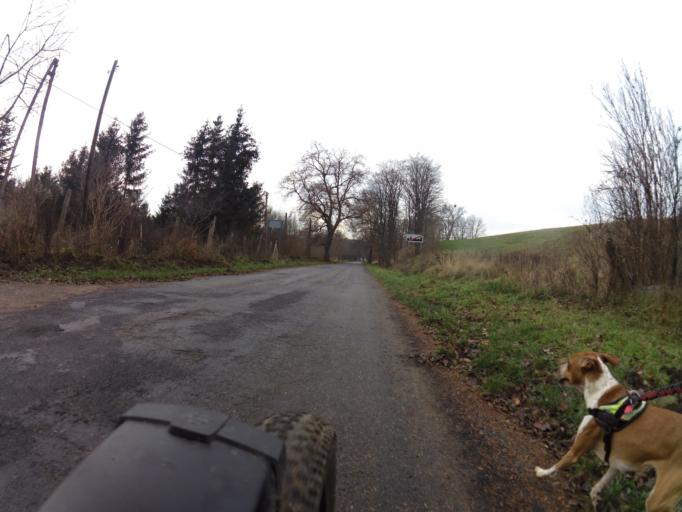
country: PL
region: West Pomeranian Voivodeship
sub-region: Powiat koszalinski
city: Polanow
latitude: 54.0647
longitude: 16.6604
